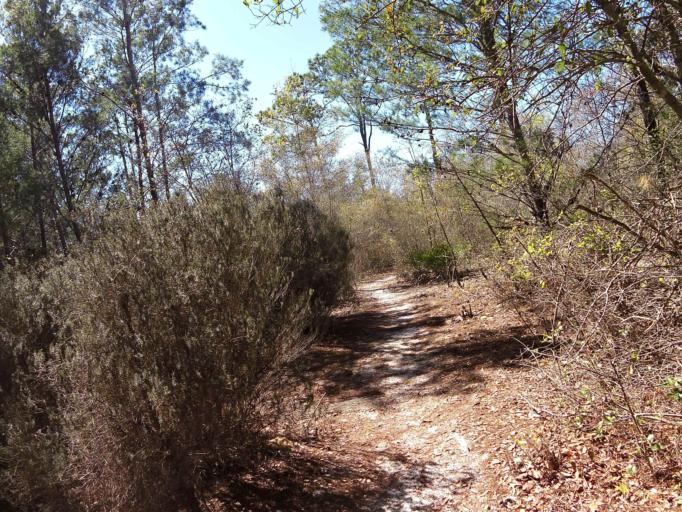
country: US
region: Florida
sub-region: Clay County
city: Keystone Heights
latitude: 29.8385
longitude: -81.9846
